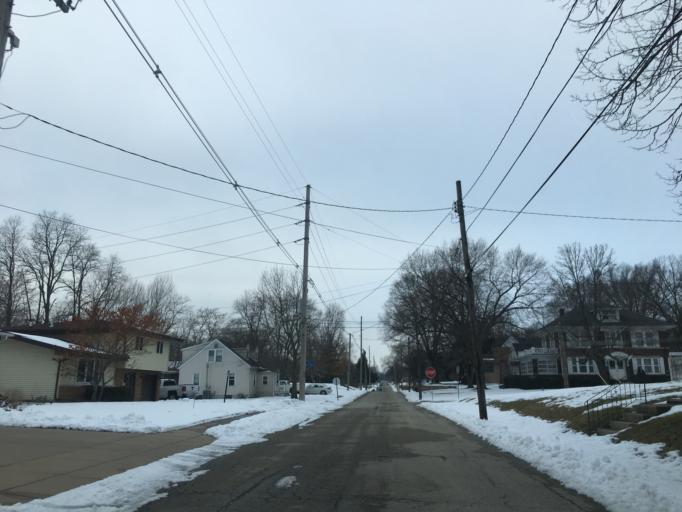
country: US
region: Illinois
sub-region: LaSalle County
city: Peru
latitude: 41.3249
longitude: -89.1259
